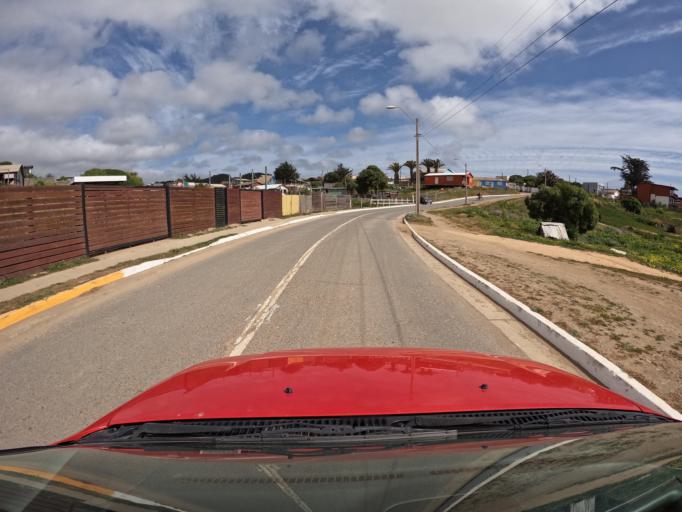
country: CL
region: O'Higgins
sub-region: Provincia de Colchagua
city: Santa Cruz
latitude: -34.3881
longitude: -72.0177
